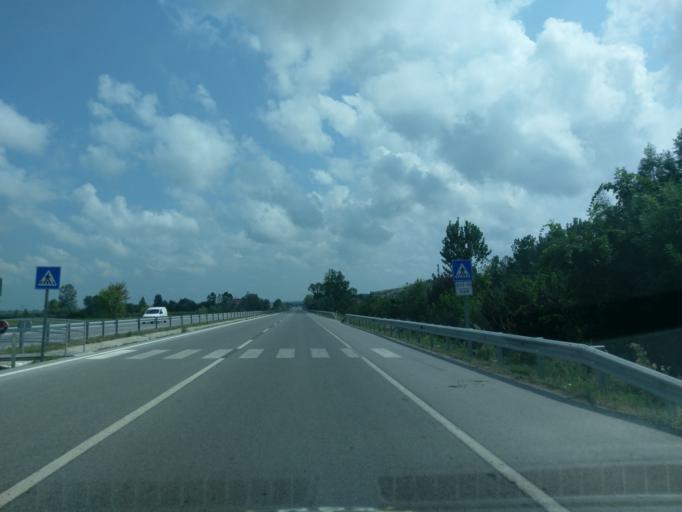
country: TR
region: Samsun
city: Alacam
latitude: 41.6113
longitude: 35.7154
